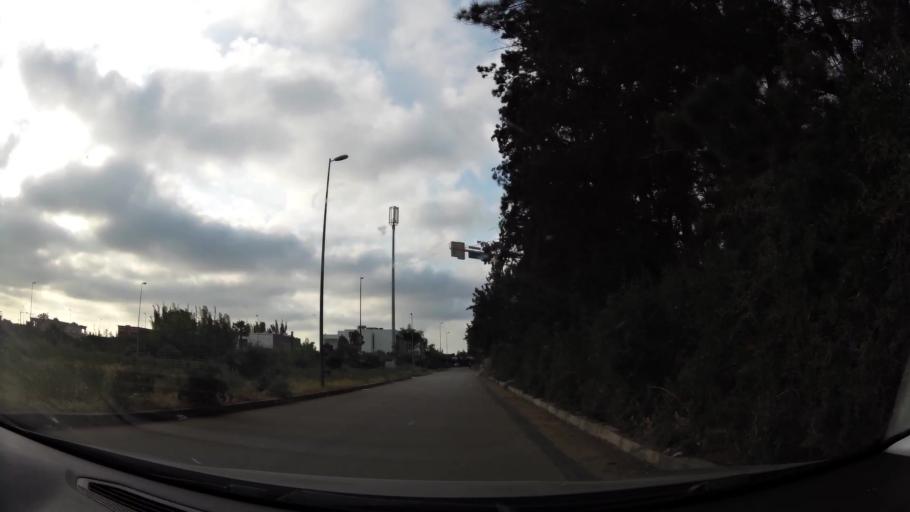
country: MA
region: Rabat-Sale-Zemmour-Zaer
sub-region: Rabat
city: Rabat
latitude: 33.9496
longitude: -6.8426
